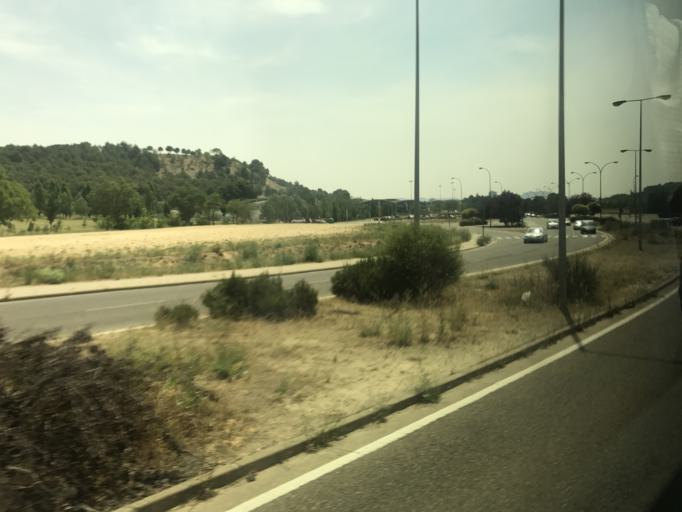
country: ES
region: Castille and Leon
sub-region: Provincia de Valladolid
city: Zaratan
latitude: 41.6502
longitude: -4.7604
